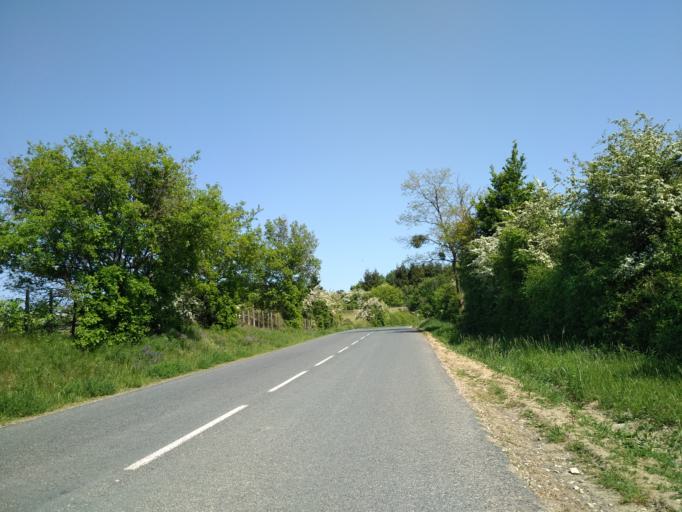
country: FR
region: Rhone-Alpes
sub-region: Departement du Rhone
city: Fontaines-sur-Saone
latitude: 45.8253
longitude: 4.8165
